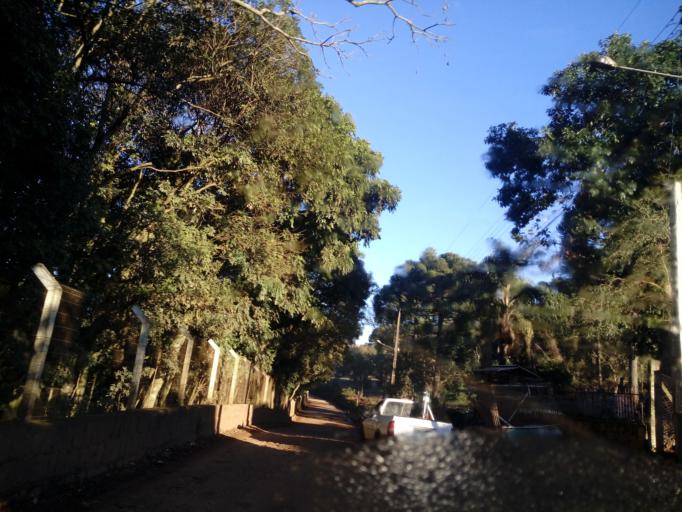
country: BR
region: Santa Catarina
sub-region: Chapeco
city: Chapeco
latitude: -27.1249
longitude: -52.6232
